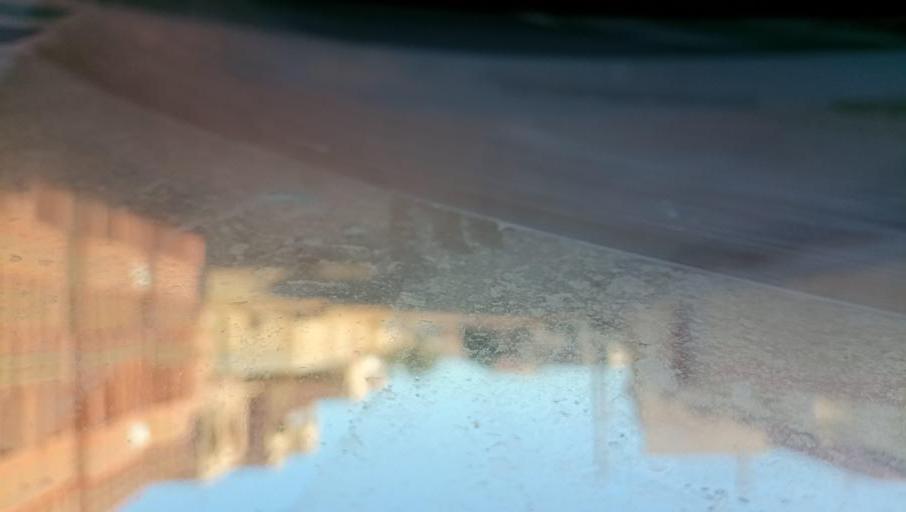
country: TN
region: Tataouine
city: Tataouine
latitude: 32.9879
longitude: 10.4594
